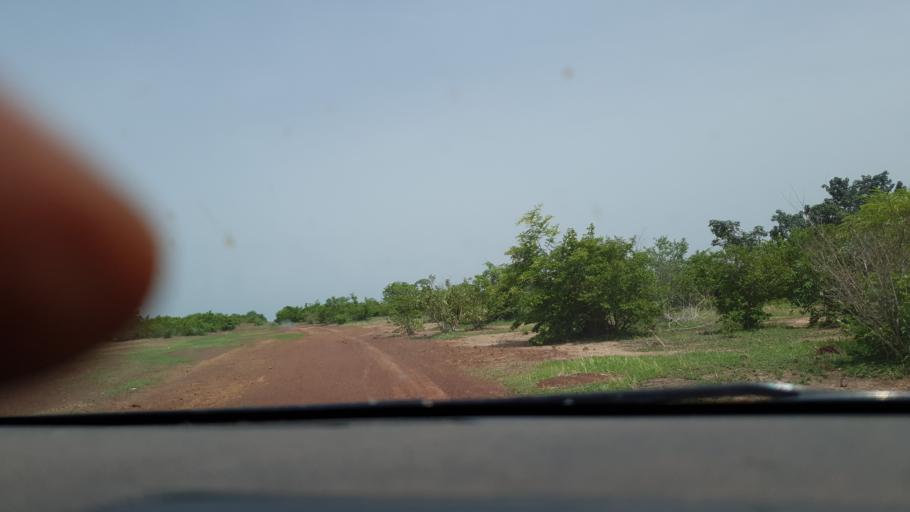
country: ML
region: Koulikoro
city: Koulikoro
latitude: 12.6657
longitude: -7.2276
